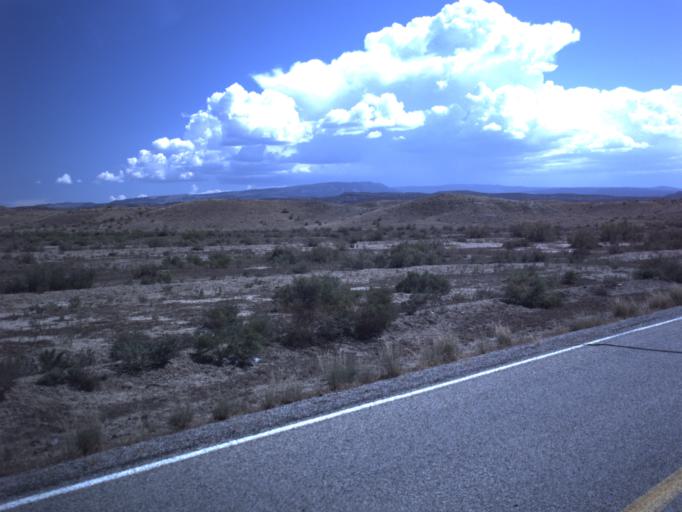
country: US
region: Utah
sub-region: Grand County
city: Moab
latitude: 38.8682
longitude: -109.2963
